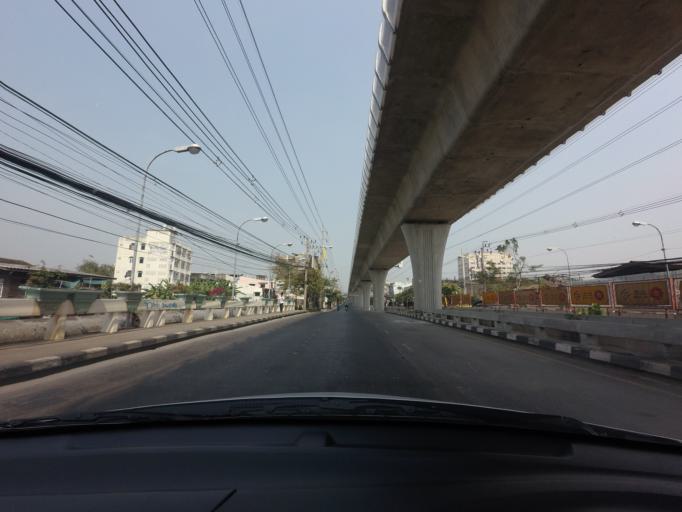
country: TH
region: Bangkok
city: Bangkok Yai
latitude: 13.7431
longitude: 100.4704
